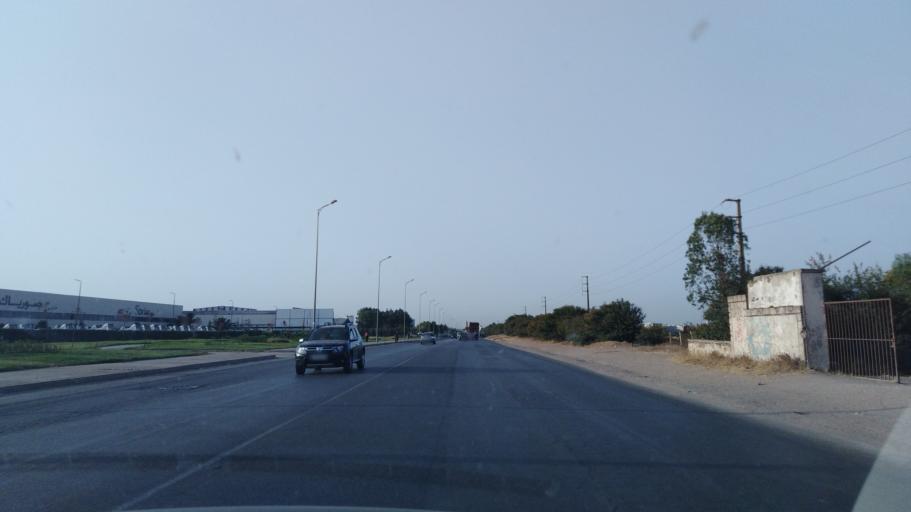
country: MA
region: Chaouia-Ouardigha
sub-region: Settat Province
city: Berrechid
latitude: 33.2476
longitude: -7.5856
